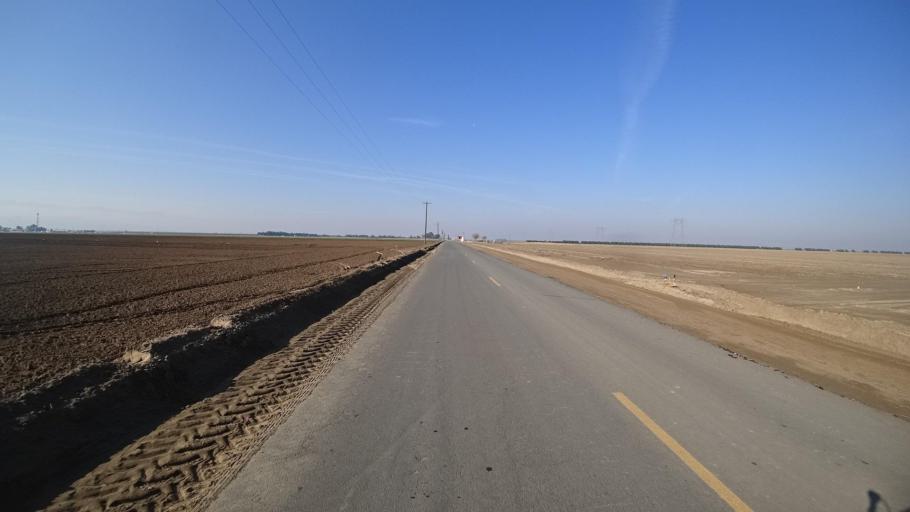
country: US
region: California
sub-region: Kern County
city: Weedpatch
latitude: 35.1218
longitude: -118.9074
